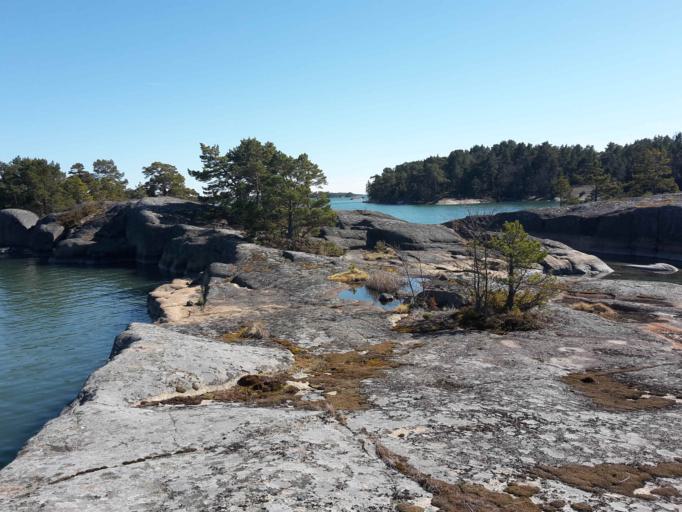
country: FI
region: Varsinais-Suomi
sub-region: Vakka-Suomi
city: Kustavi
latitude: 60.5820
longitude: 21.2161
